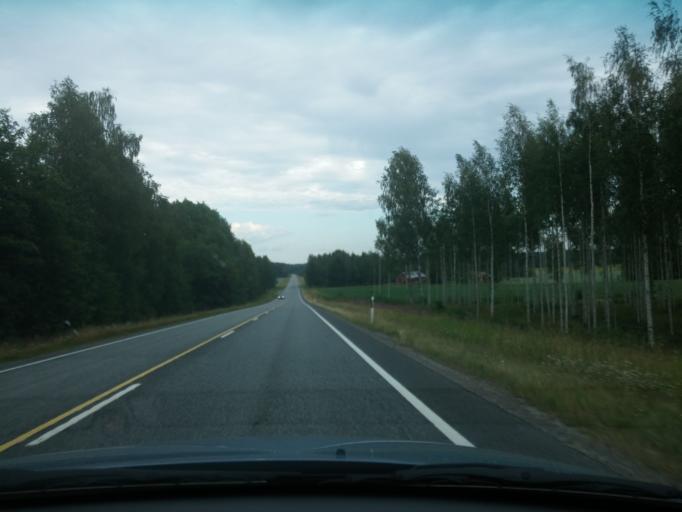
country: FI
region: Haeme
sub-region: Haemeenlinna
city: Tervakoski
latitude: 60.7395
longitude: 24.5995
